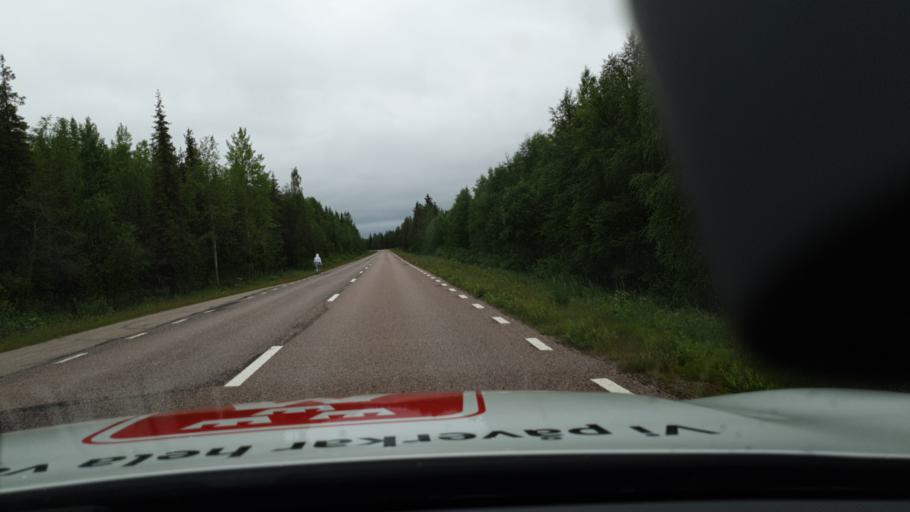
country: FI
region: Lapland
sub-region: Tunturi-Lappi
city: Kolari
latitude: 67.0799
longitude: 23.6605
